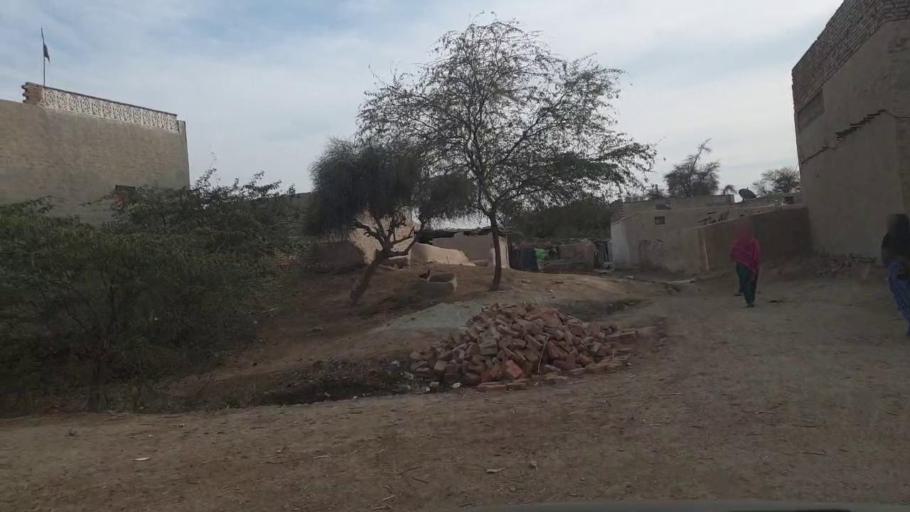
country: PK
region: Sindh
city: Shahpur Chakar
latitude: 26.1255
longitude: 68.5690
